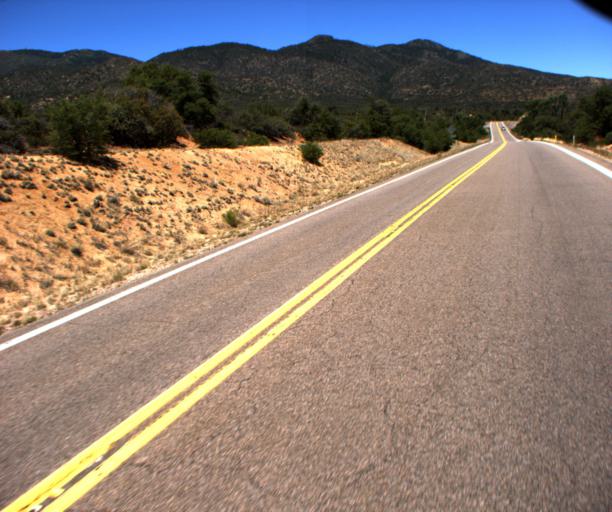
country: US
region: Arizona
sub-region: Gila County
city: Globe
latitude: 33.2415
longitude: -110.7831
